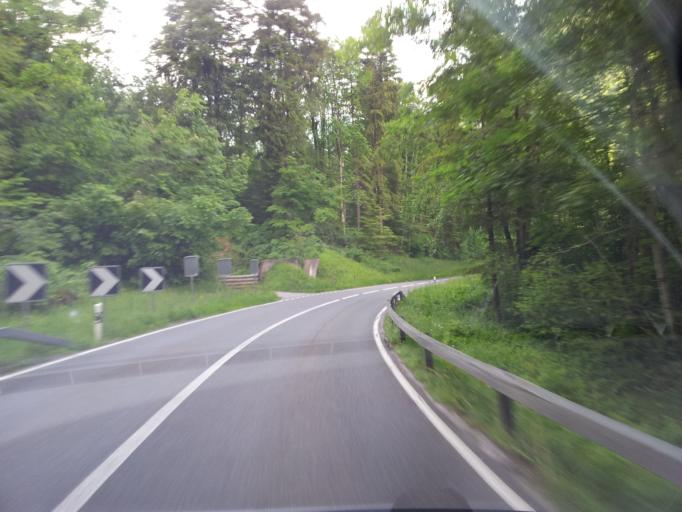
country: CH
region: Bern
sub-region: Interlaken-Oberhasli District
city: Lauterbrunnen
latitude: 46.6341
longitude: 7.8944
